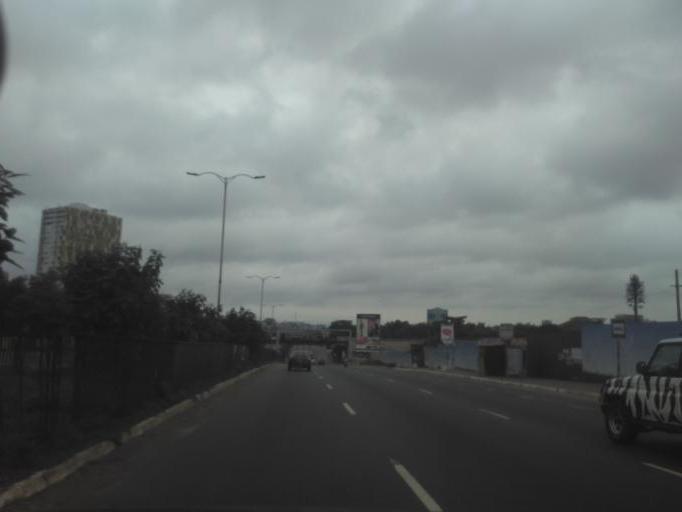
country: GH
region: Greater Accra
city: Medina Estates
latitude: 5.6170
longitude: -0.1760
